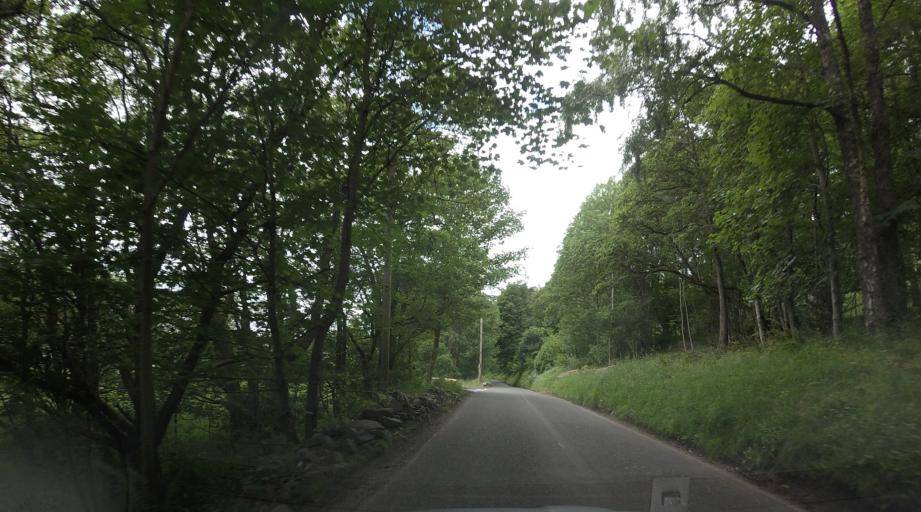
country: GB
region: Scotland
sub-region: Perth and Kinross
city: Aberfeldy
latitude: 56.7021
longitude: -4.1812
